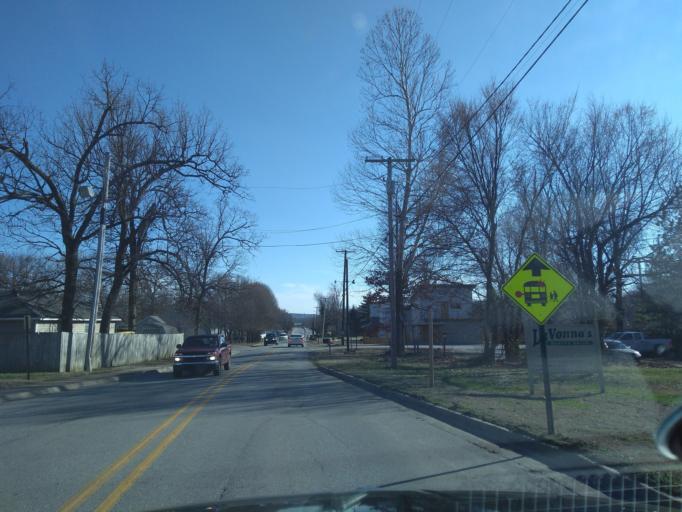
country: US
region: Arkansas
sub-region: Washington County
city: Johnson
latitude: 36.1326
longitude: -94.1630
